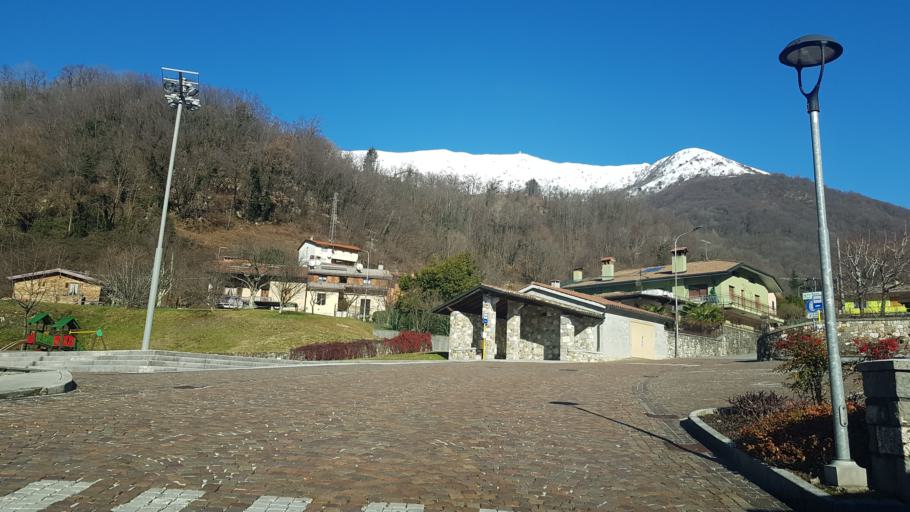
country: IT
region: Friuli Venezia Giulia
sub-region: Provincia di Udine
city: Isola
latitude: 46.2568
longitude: 13.1807
